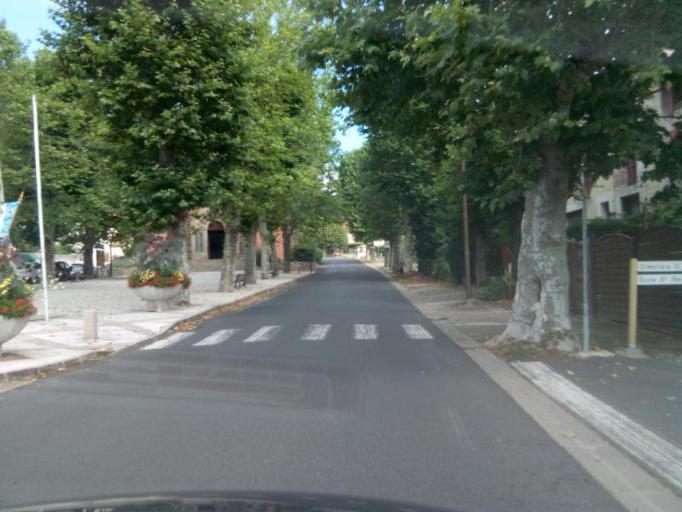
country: FR
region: Auvergne
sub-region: Departement de la Haute-Loire
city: Vorey
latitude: 45.1879
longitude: 3.9108
